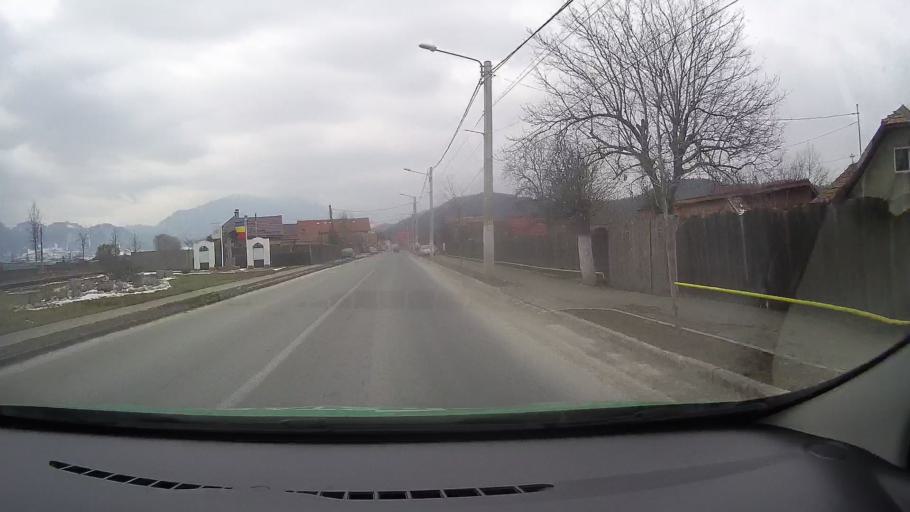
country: RO
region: Brasov
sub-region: Comuna Zarnesti
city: Tohanu Nou
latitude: 45.5761
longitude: 25.3763
